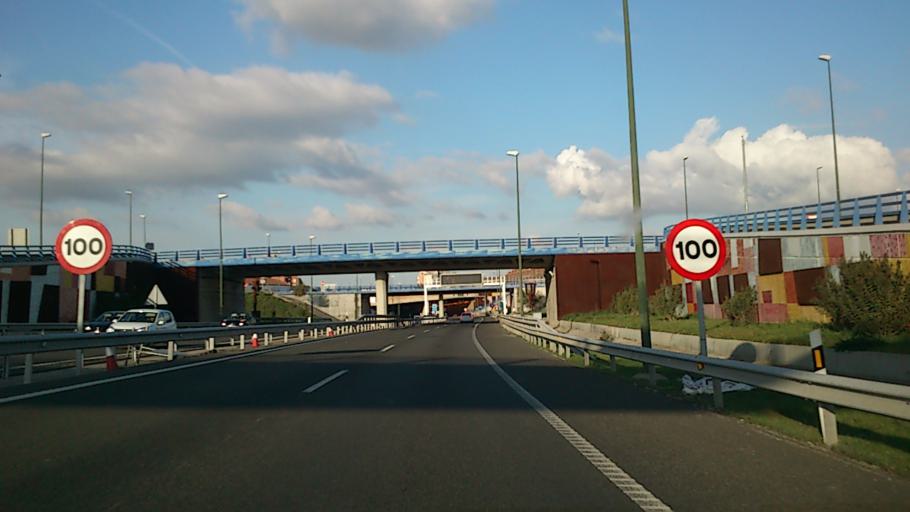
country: ES
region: Aragon
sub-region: Provincia de Zaragoza
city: Zaragoza
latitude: 41.6642
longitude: -0.8387
